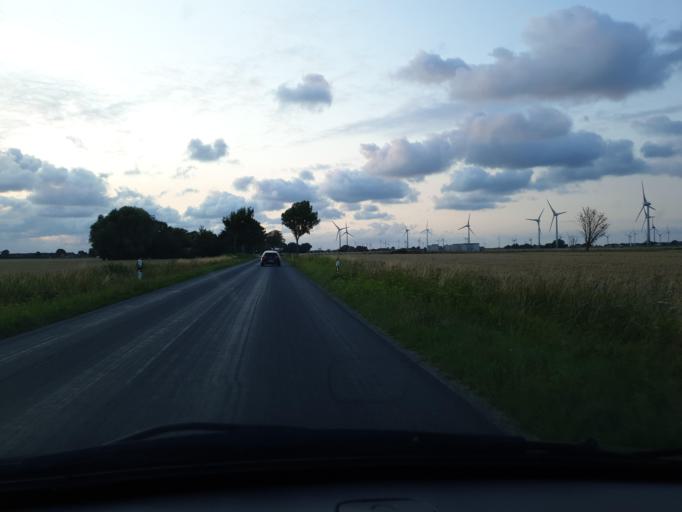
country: DE
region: Schleswig-Holstein
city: Kronprinzenkoog
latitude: 53.9679
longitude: 8.9278
